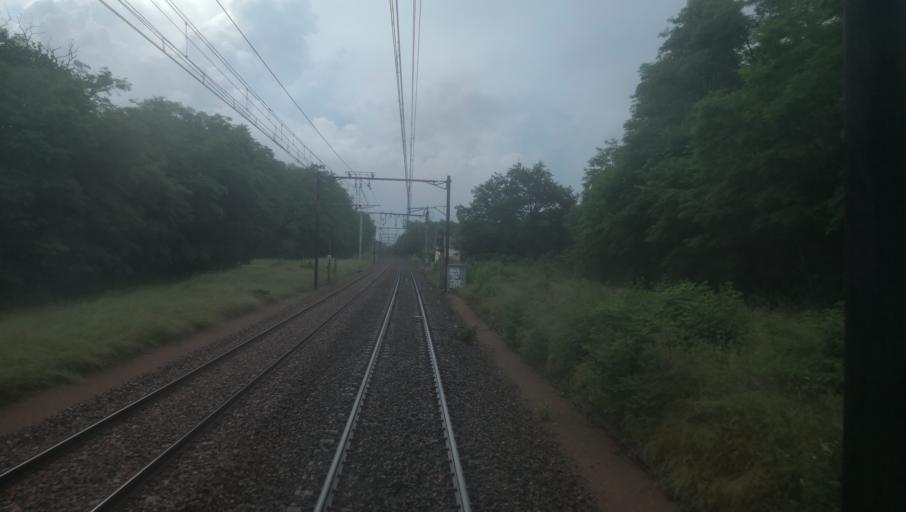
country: FR
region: Centre
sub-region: Departement du Loiret
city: Saint-Cyr-en-Val
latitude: 47.8267
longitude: 1.9487
